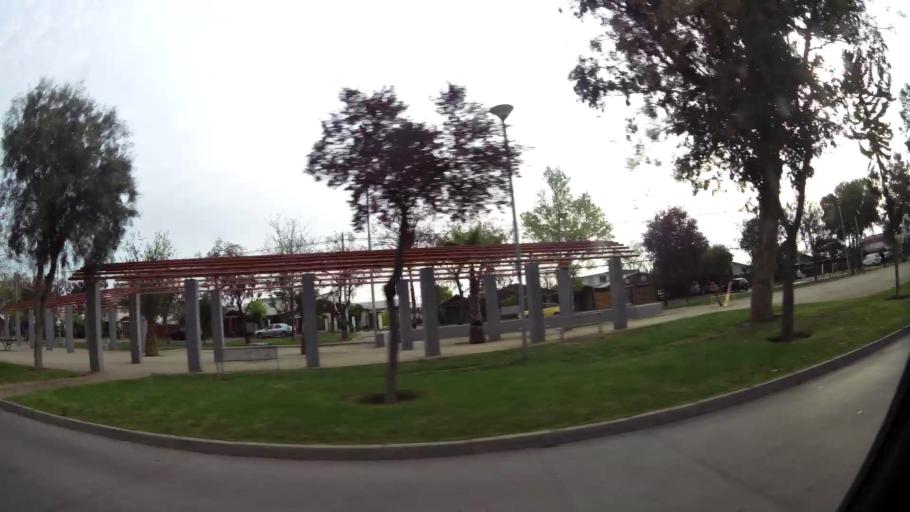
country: CL
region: Santiago Metropolitan
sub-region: Provincia de Maipo
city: San Bernardo
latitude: -33.5344
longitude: -70.7715
